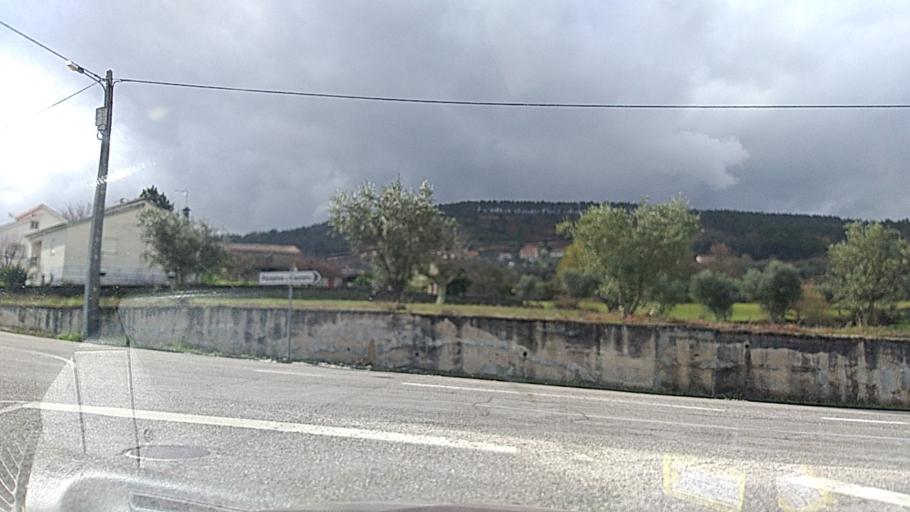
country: PT
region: Viseu
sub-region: Satao
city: Satao
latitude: 40.6569
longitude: -7.6587
